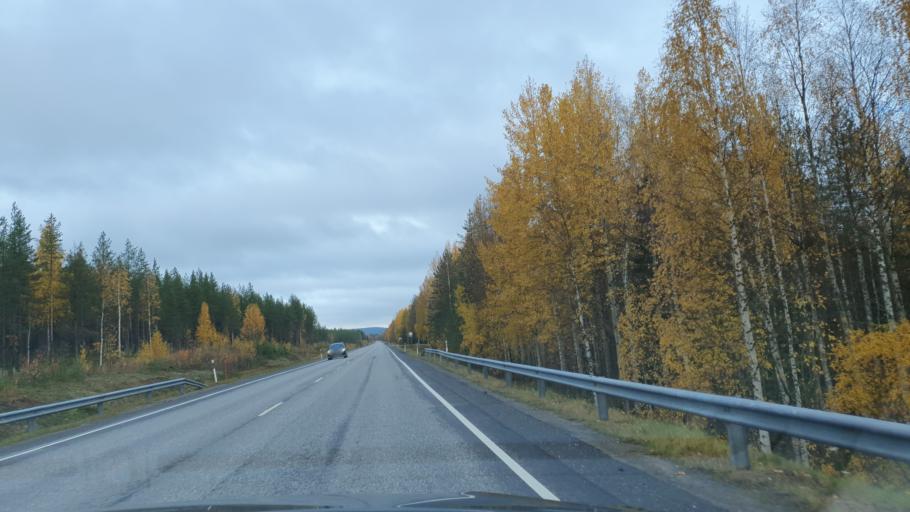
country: FI
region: Lapland
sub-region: Rovaniemi
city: Rovaniemi
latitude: 66.5594
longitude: 25.6454
